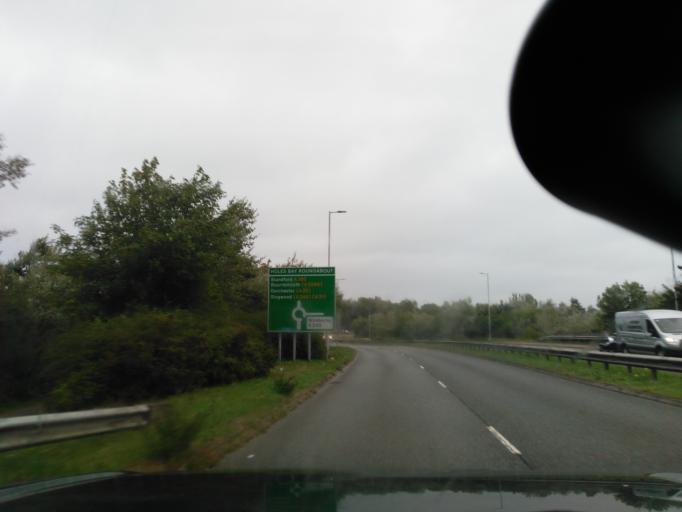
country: GB
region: England
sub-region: Poole
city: Poole
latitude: 50.7301
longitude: -1.9910
